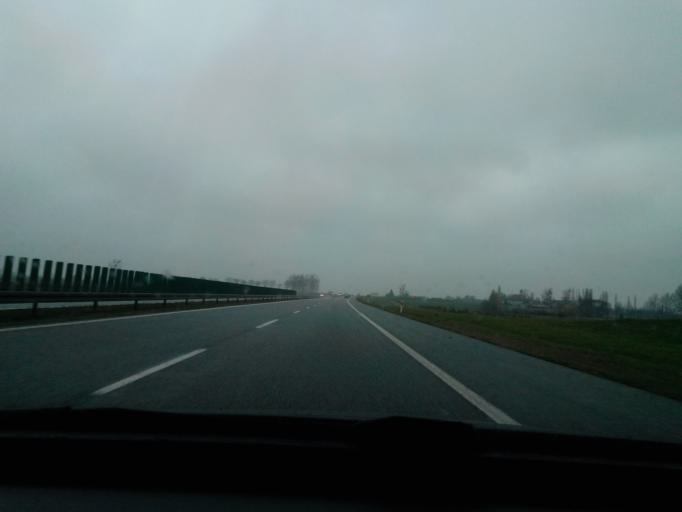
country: PL
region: Pomeranian Voivodeship
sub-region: Powiat gdanski
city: Pszczolki
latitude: 54.1281
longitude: 18.6798
